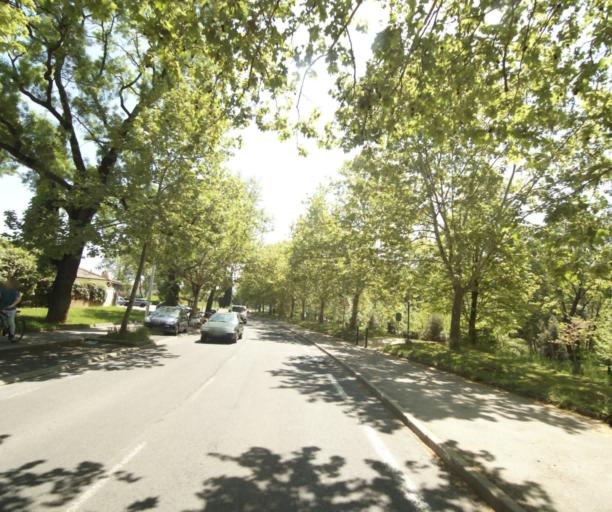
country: FR
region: Languedoc-Roussillon
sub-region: Departement de l'Herault
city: Saint-Jean-de-Vedas
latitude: 43.5970
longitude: 3.8356
